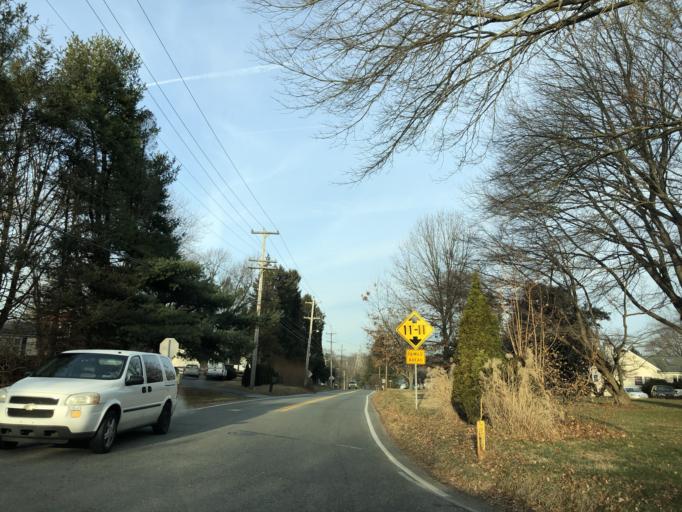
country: US
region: Pennsylvania
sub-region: Chester County
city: Exton
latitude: 40.0139
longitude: -75.5999
